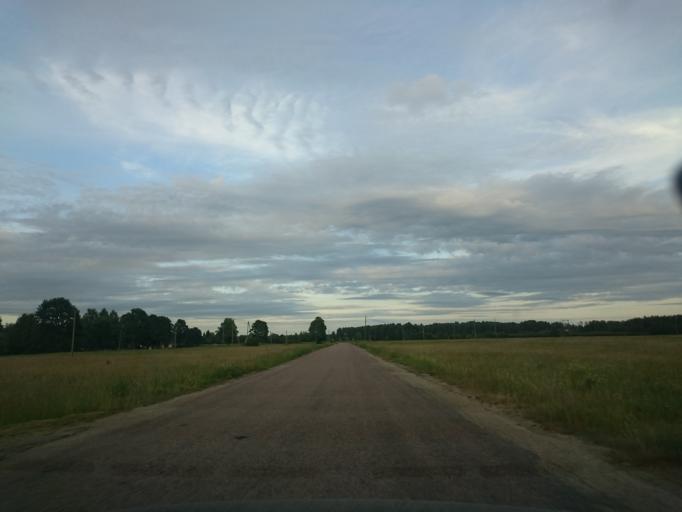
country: LV
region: Ropazu
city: Ropazi
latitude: 56.9693
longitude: 24.6554
